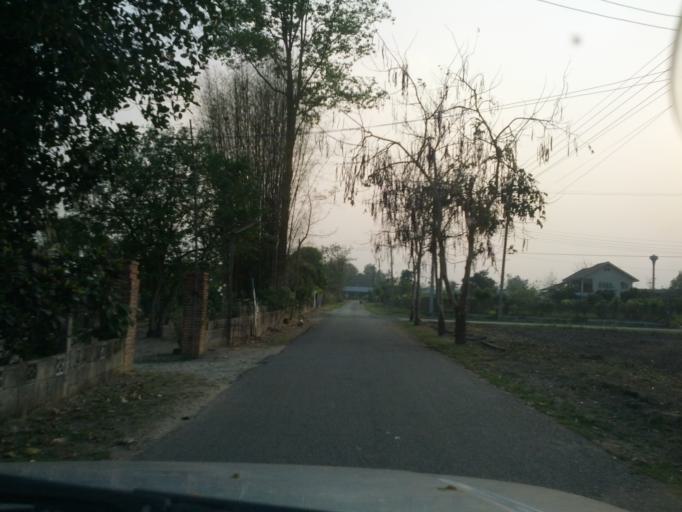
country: TH
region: Chiang Mai
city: San Sai
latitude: 18.9277
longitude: 99.0158
